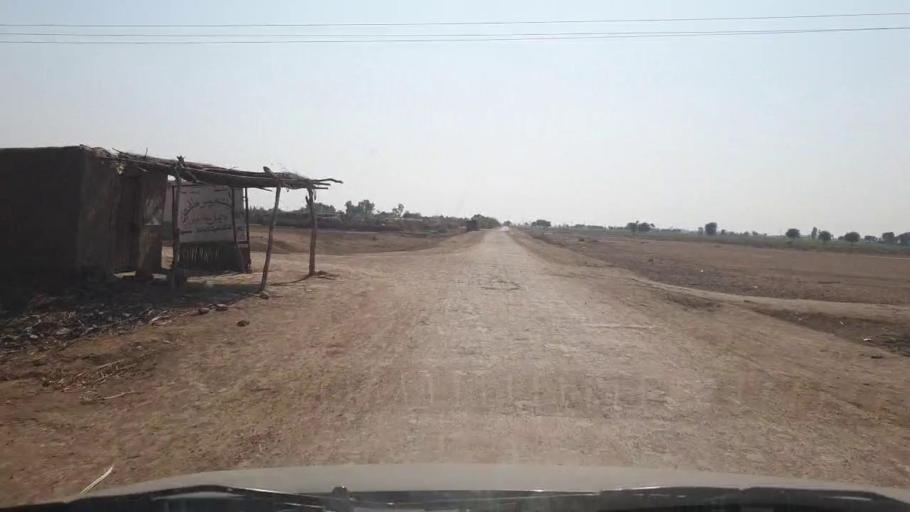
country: PK
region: Sindh
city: Samaro
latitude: 25.1802
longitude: 69.3356
